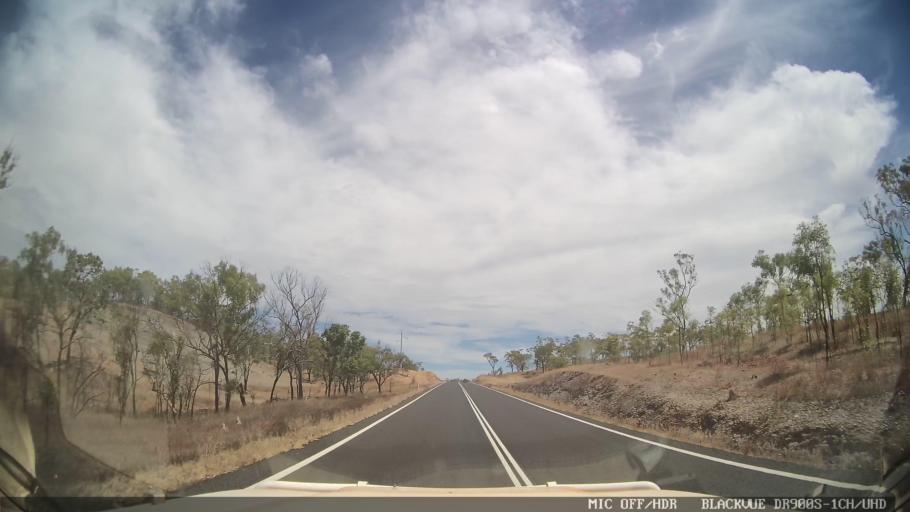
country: AU
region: Queensland
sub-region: Cairns
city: Port Douglas
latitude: -16.1399
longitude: 144.7728
